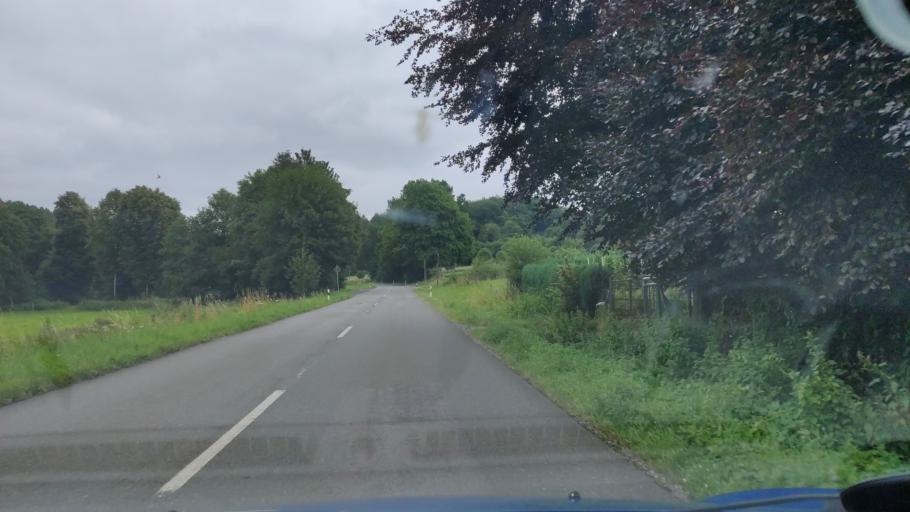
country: DE
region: Lower Saxony
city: Holzminden
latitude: 51.8092
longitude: 9.4773
